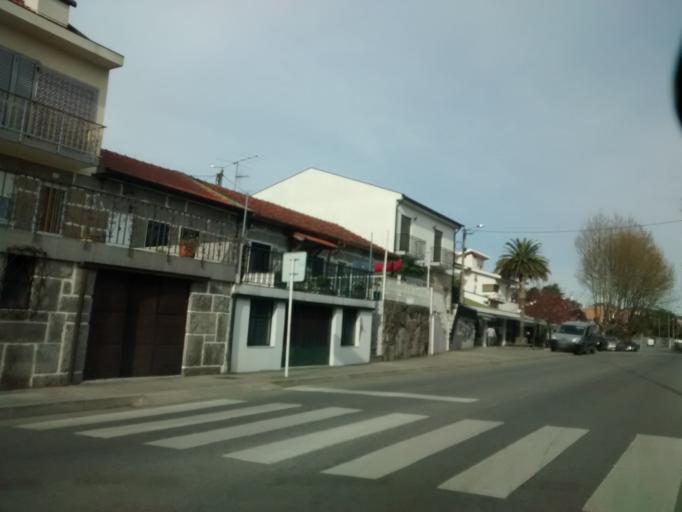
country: PT
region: Braga
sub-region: Guimaraes
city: Guimaraes
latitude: 41.4559
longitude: -8.2961
